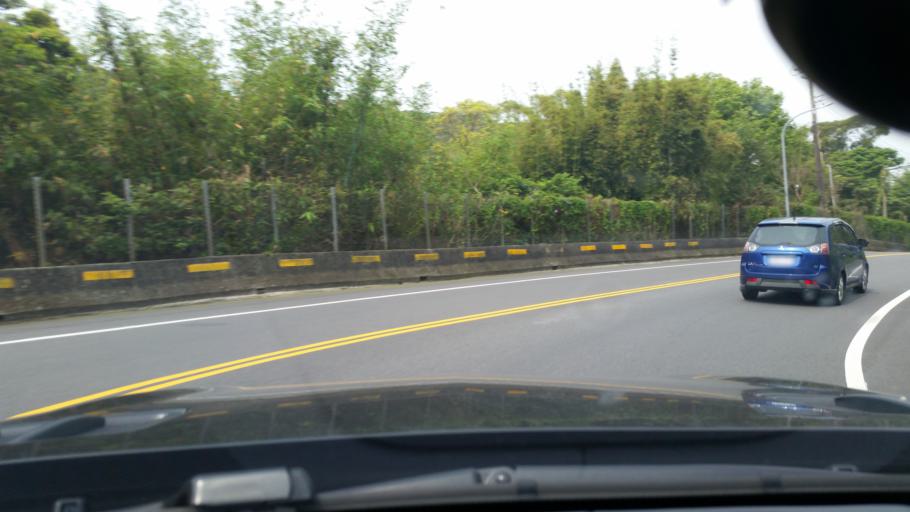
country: TW
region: Taiwan
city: Taoyuan City
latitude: 25.0606
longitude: 121.3148
